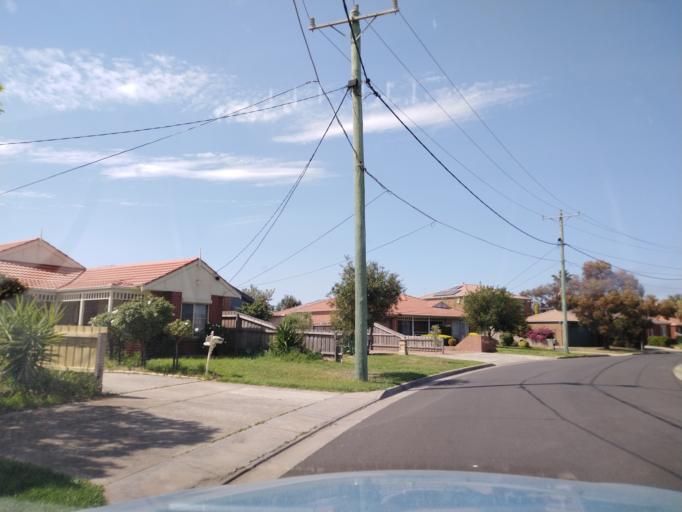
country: AU
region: Victoria
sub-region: Wyndham
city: Hoppers Crossing
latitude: -37.8585
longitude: 144.7092
